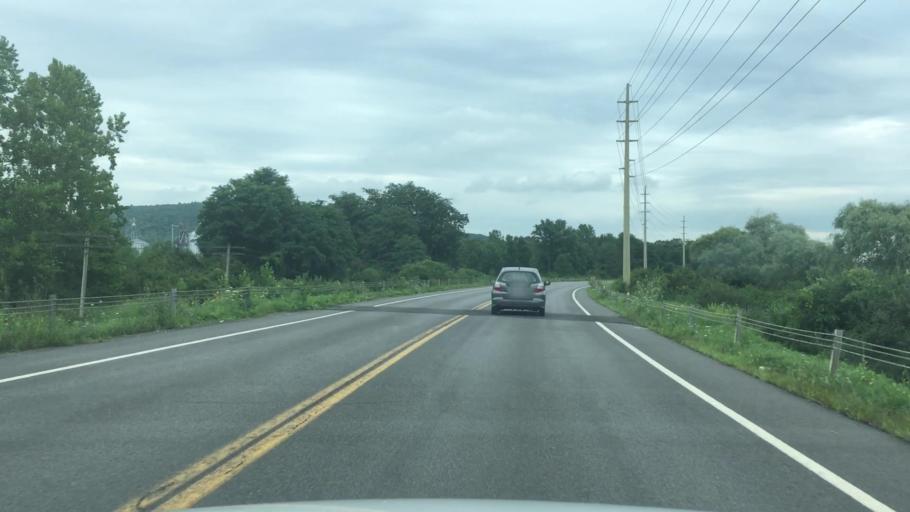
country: US
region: New York
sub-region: Otsego County
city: West End
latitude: 42.4436
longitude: -75.1014
